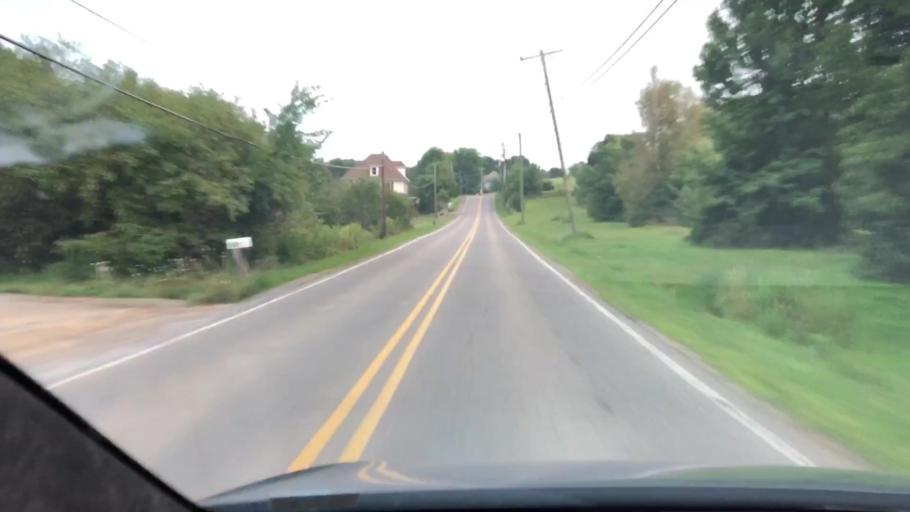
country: US
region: Pennsylvania
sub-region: Butler County
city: Shanor-Northvue
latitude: 40.8982
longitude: -79.9287
